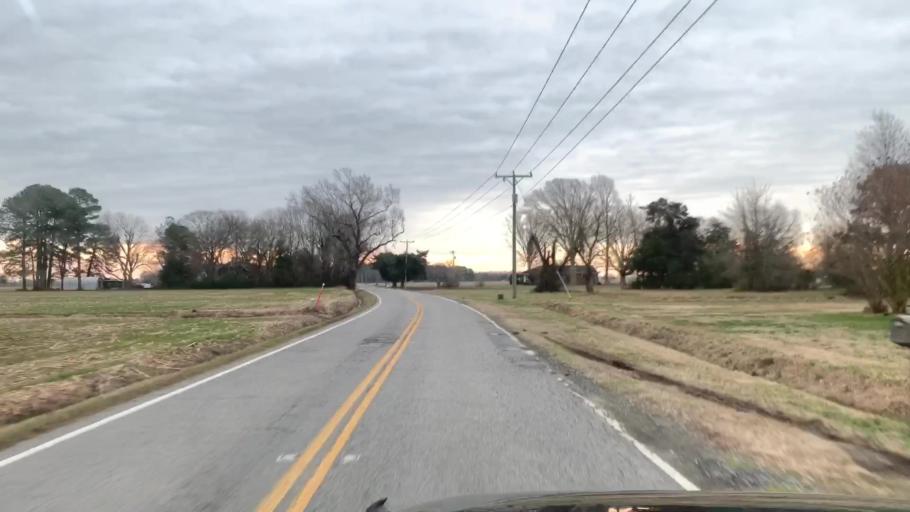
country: US
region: North Carolina
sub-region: Currituck County
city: Moyock
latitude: 36.6354
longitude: -76.1901
